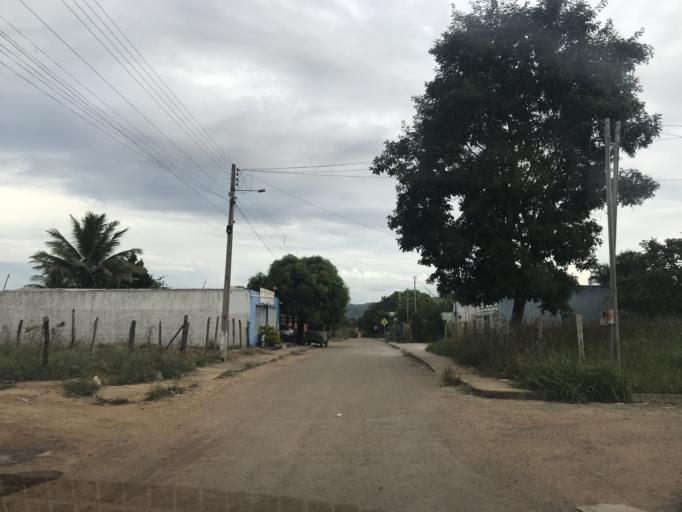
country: BR
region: Goias
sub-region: Padre Bernardo
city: Padre Bernardo
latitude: -15.3591
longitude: -48.2286
